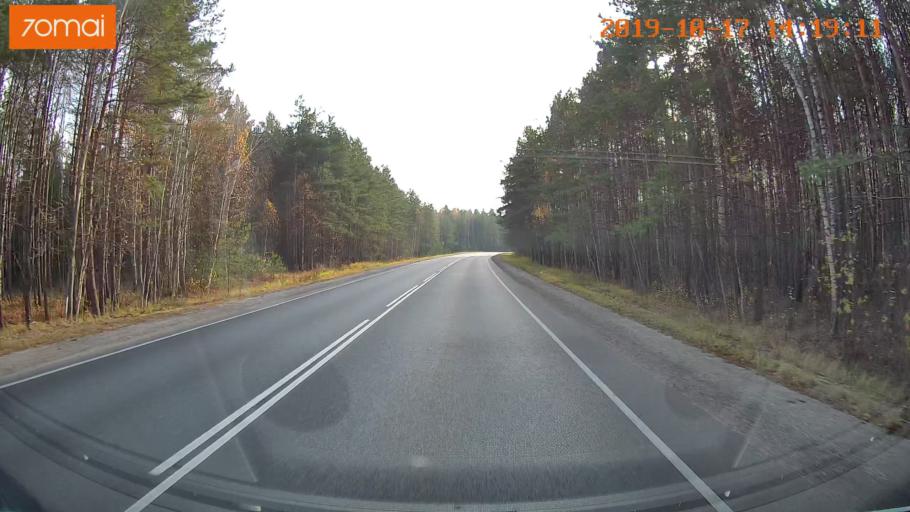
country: RU
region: Rjazan
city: Spas-Klepiki
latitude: 55.0530
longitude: 40.0236
